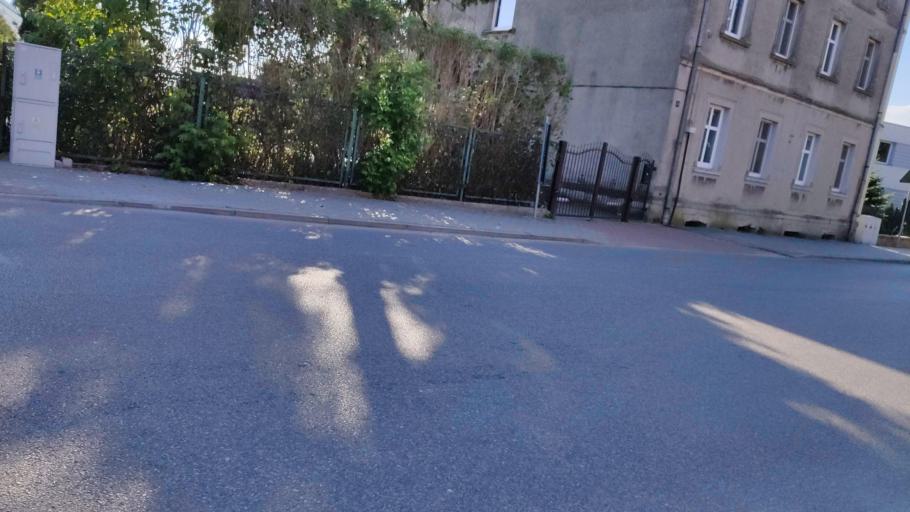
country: PL
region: Kujawsko-Pomorskie
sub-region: Powiat zninski
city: Znin
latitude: 52.8448
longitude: 17.7268
